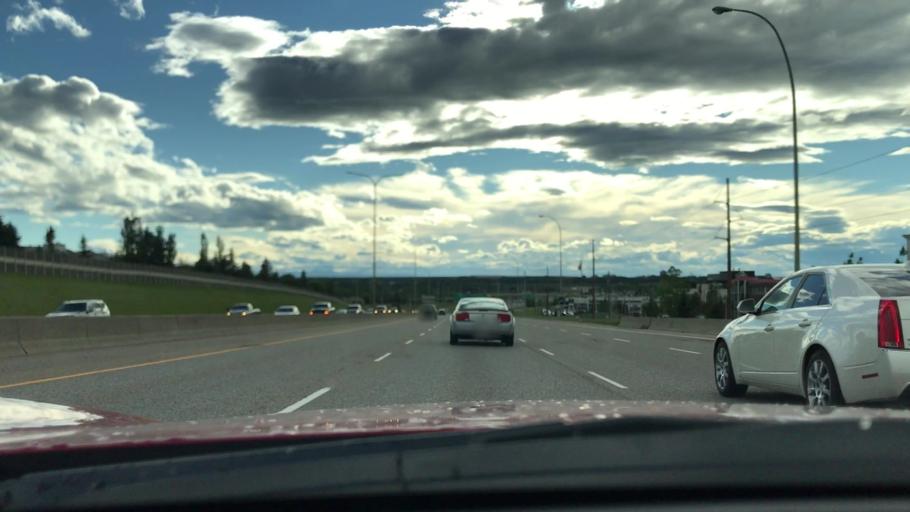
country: CA
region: Alberta
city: Calgary
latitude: 50.9470
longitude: -113.9909
